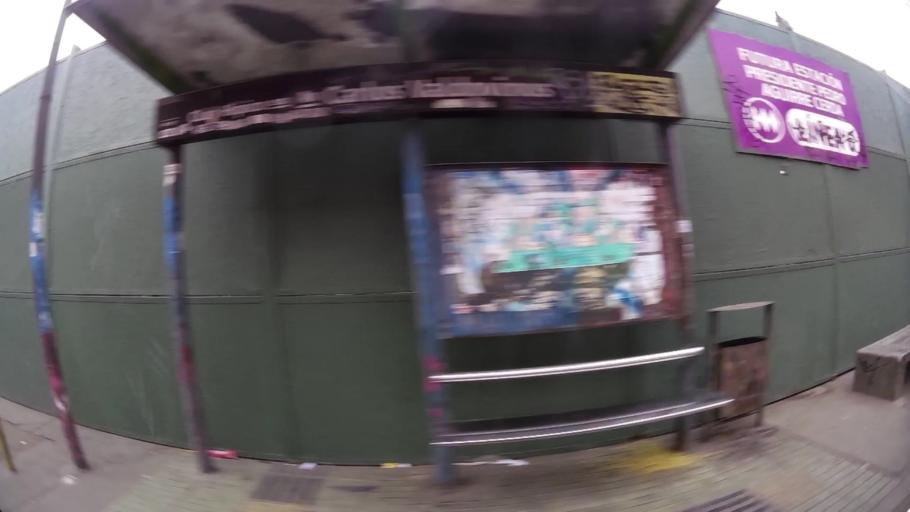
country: CL
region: Santiago Metropolitan
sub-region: Provincia de Santiago
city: Santiago
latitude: -33.4784
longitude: -70.6649
